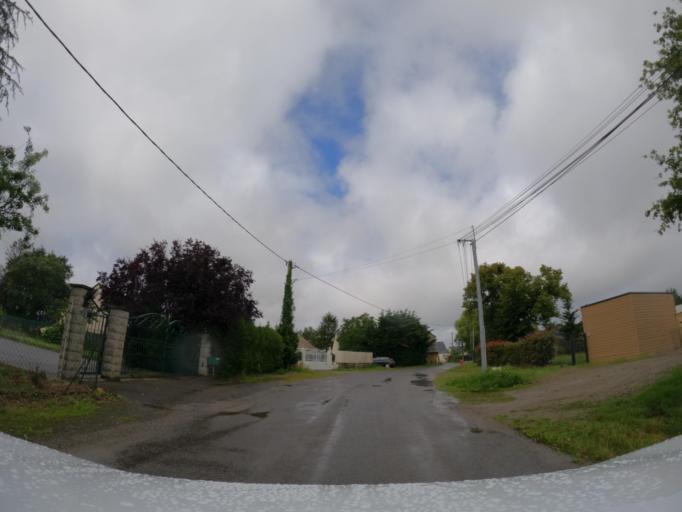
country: FR
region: Pays de la Loire
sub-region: Departement de la Loire-Atlantique
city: Ligne
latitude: 47.3982
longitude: -1.3782
